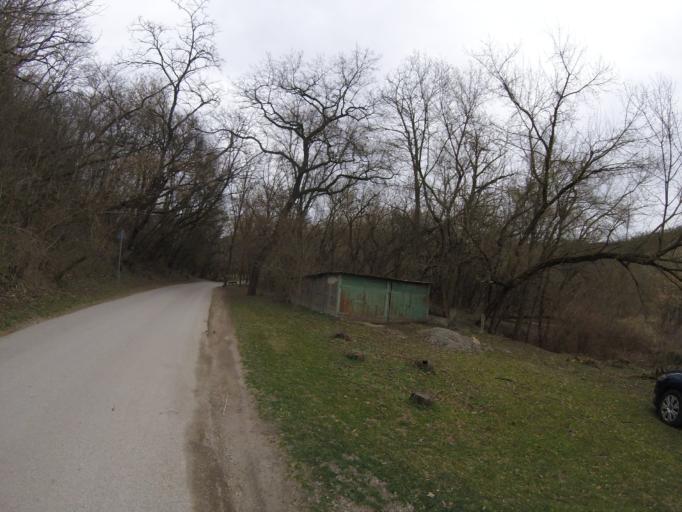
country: HU
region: Pest
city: Szob
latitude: 47.8036
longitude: 18.8075
